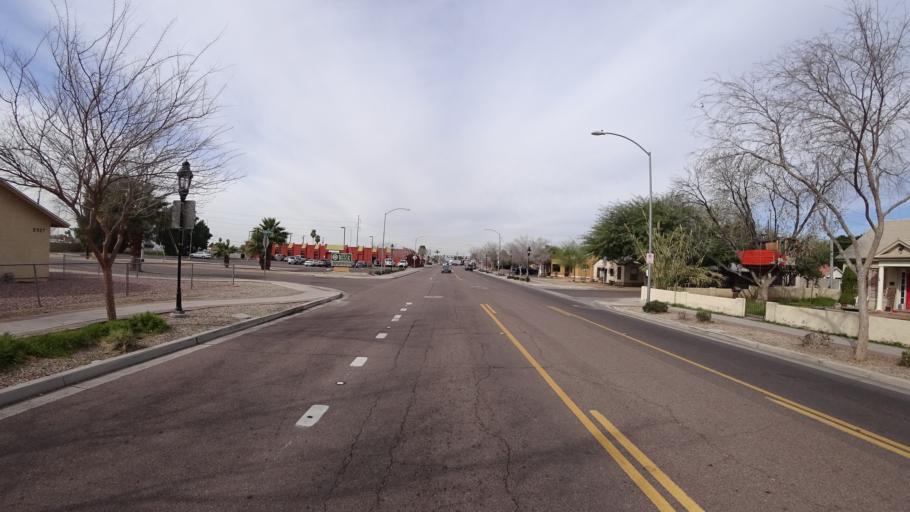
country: US
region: Arizona
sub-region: Maricopa County
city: Glendale
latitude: 33.5422
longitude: -112.1875
